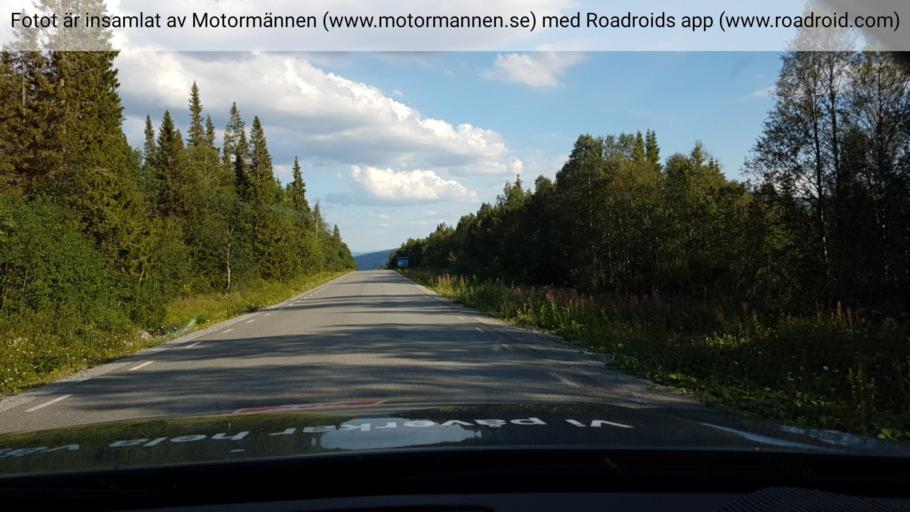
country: SE
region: Jaemtland
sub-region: Are Kommun
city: Are
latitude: 63.4165
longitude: 13.0248
